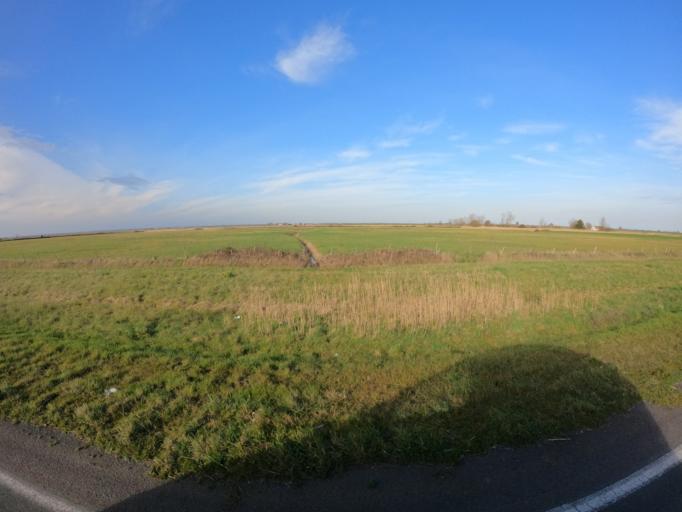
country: FR
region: Pays de la Loire
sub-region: Departement de la Vendee
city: Angles
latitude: 46.3528
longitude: -1.3705
